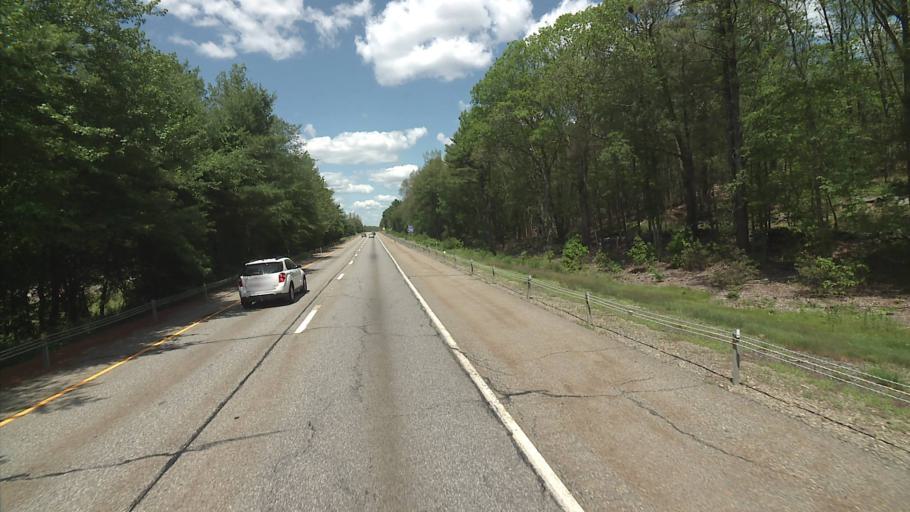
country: US
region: Massachusetts
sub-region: Worcester County
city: Webster
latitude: 42.0150
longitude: -71.8572
